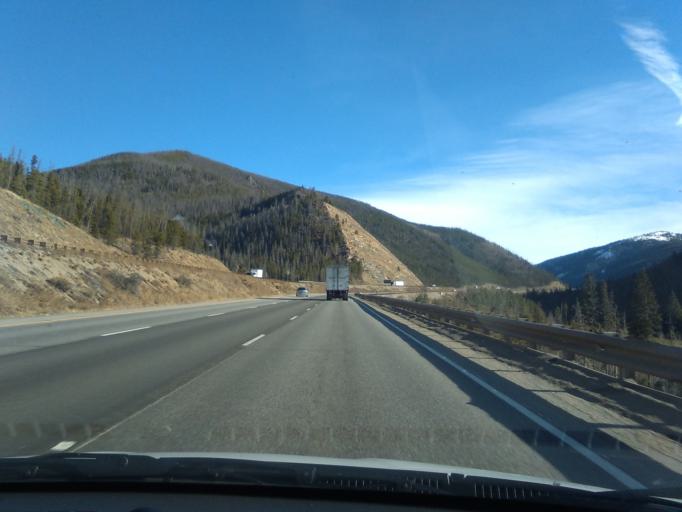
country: US
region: Colorado
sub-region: Summit County
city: Silverthorne
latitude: 39.6474
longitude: -106.0244
